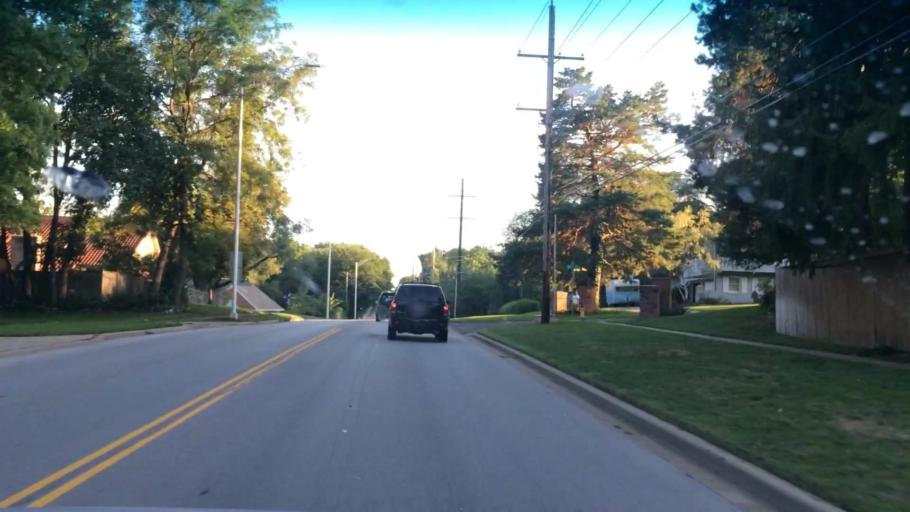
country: US
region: Kansas
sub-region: Johnson County
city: Prairie Village
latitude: 38.9754
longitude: -94.6490
